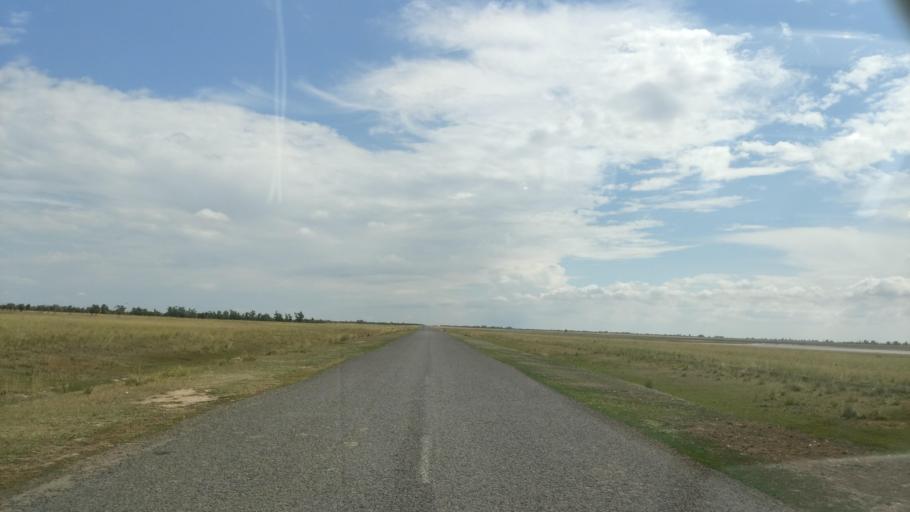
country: KZ
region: Pavlodar
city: Pavlodar
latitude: 52.6355
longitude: 76.9256
